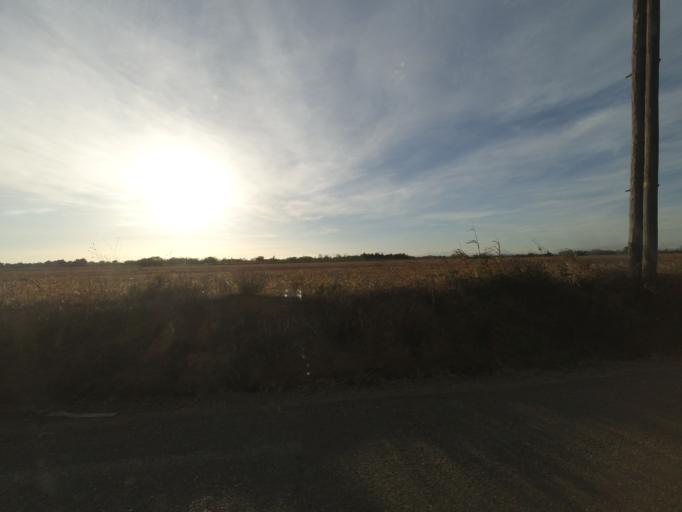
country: FR
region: Languedoc-Roussillon
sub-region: Departement du Gard
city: Le Cailar
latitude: 43.6888
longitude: 4.2314
